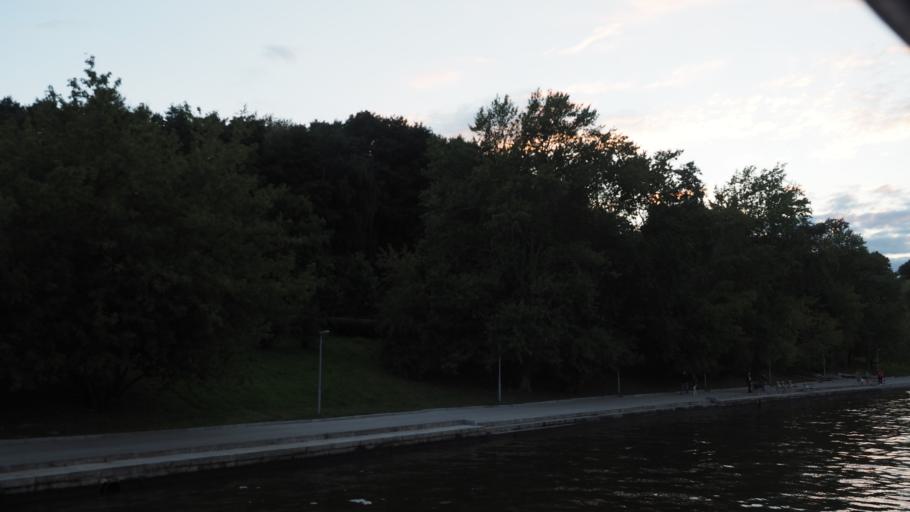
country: RU
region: Moscow
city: Luzhniki
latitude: 55.7122
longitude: 37.5464
